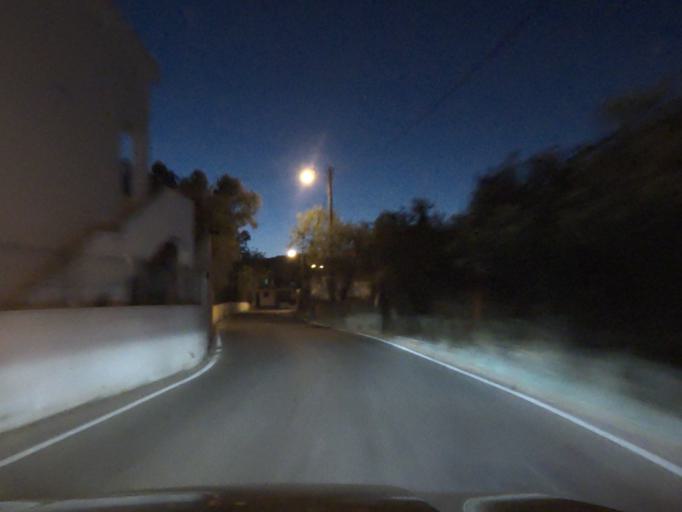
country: PT
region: Faro
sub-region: Loule
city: Loule
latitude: 37.1442
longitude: -8.0108
